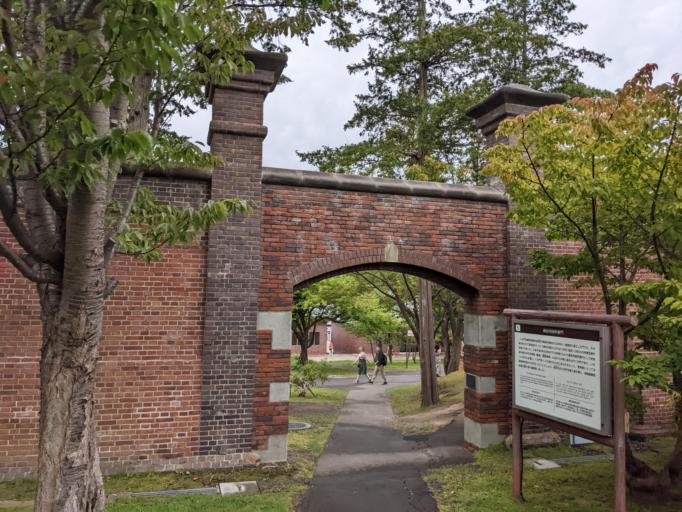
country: JP
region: Hokkaido
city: Abashiri
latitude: 43.9962
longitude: 144.2292
